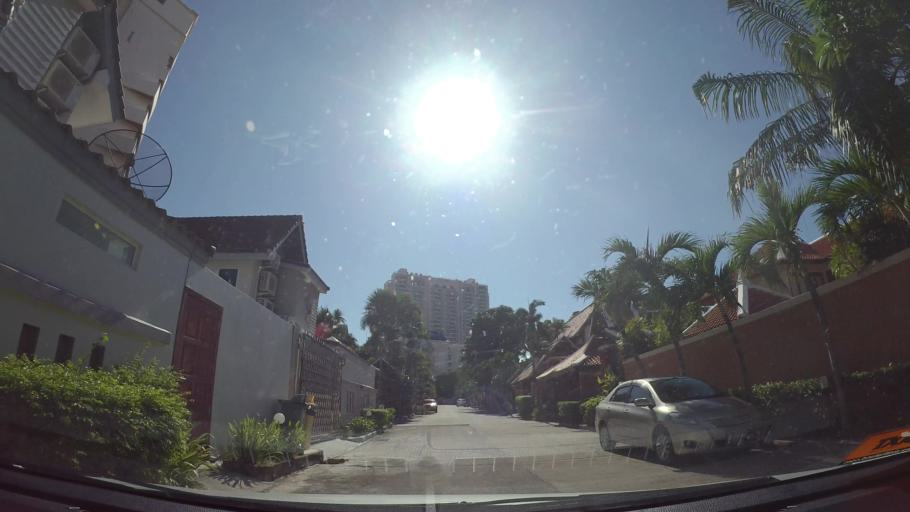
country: TH
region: Chon Buri
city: Phatthaya
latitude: 12.9068
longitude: 100.8721
